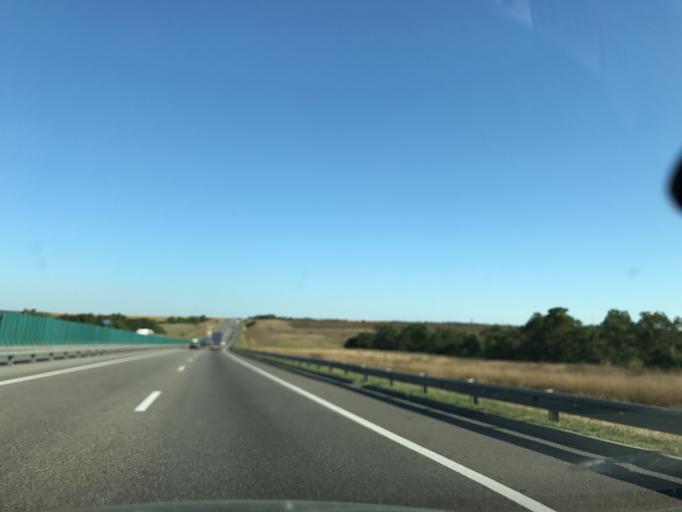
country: RU
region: Rostov
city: Glubokiy
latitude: 48.6017
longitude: 40.3541
